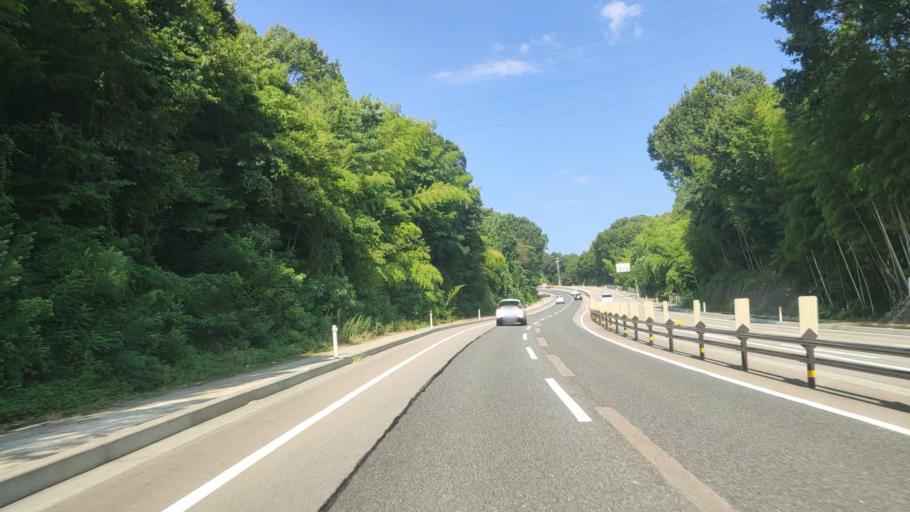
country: JP
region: Ishikawa
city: Komatsu
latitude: 36.4178
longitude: 136.5201
